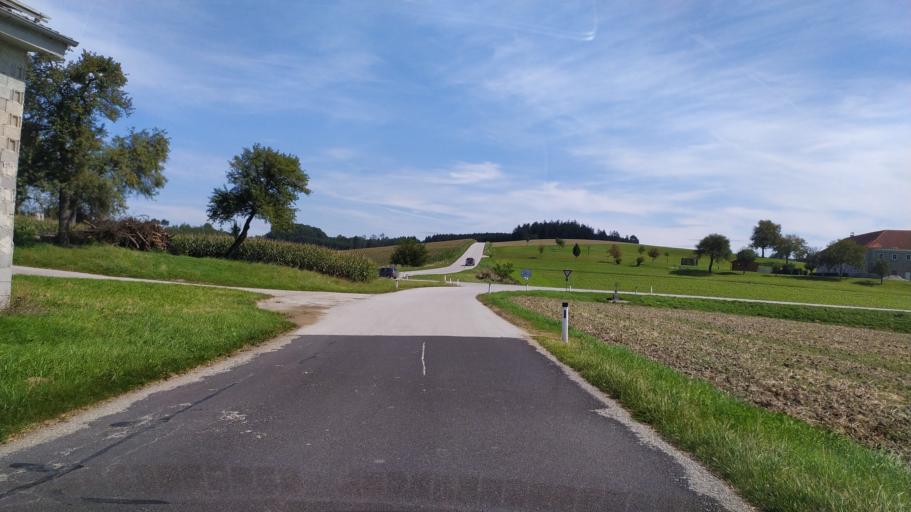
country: AT
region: Lower Austria
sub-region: Politischer Bezirk Amstetten
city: Wolfsbach
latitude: 48.1094
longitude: 14.6791
